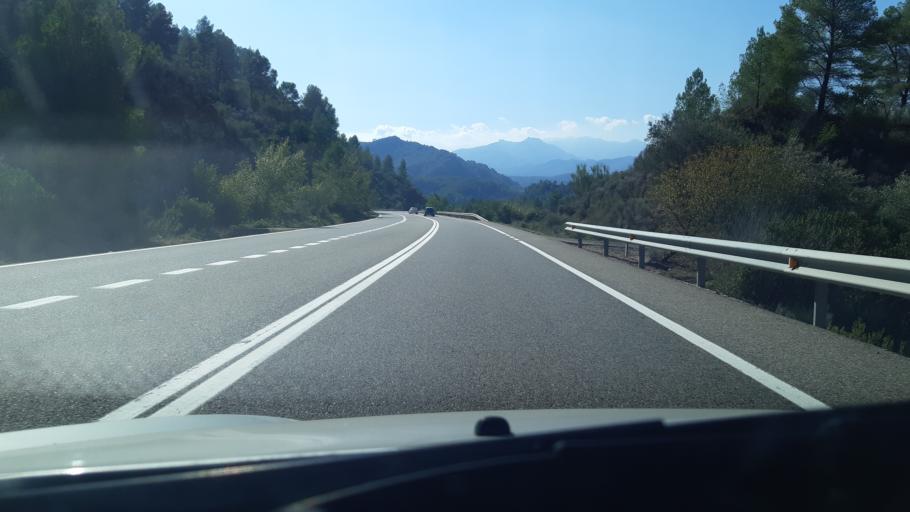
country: ES
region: Catalonia
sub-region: Provincia de Tarragona
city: Benifallet
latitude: 40.9908
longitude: 0.5427
